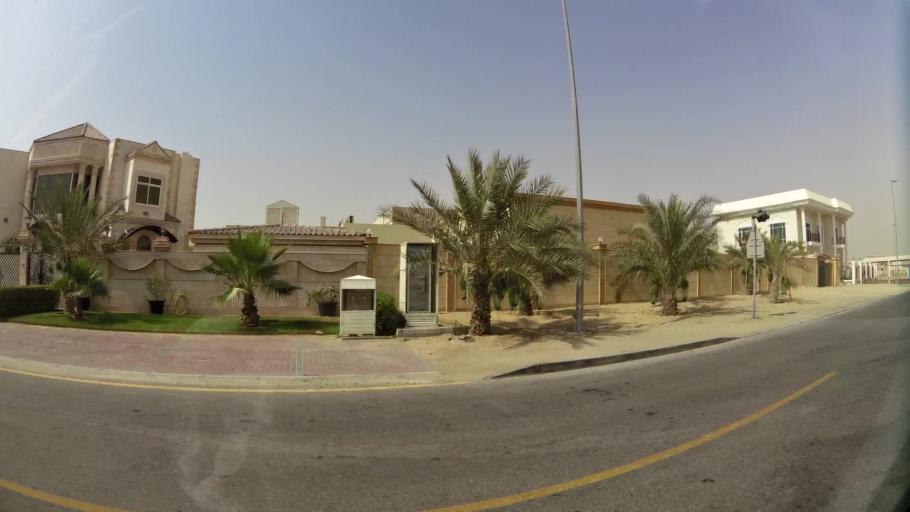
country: AE
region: Ash Shariqah
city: Sharjah
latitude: 25.2591
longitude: 55.4648
